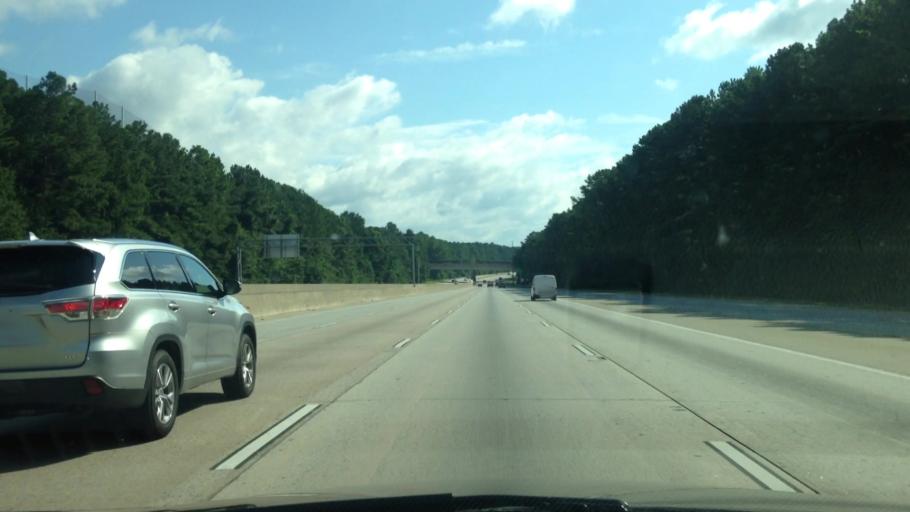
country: US
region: Georgia
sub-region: Fulton County
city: Alpharetta
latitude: 34.0426
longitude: -84.3077
